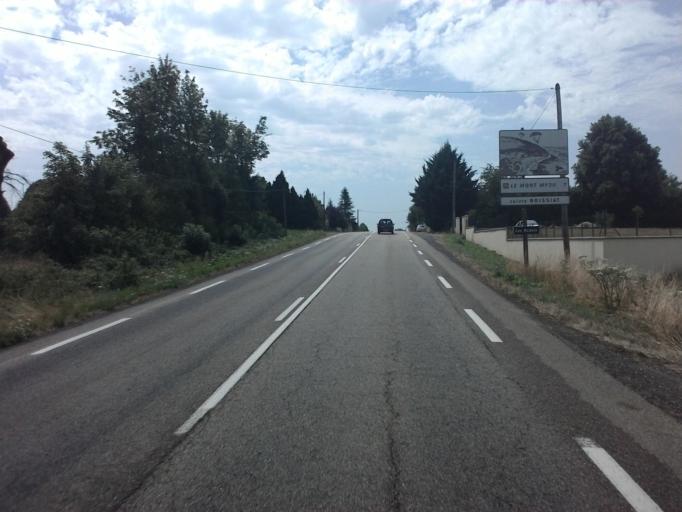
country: FR
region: Rhone-Alpes
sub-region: Departement de l'Ain
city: Coligny
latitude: 46.3389
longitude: 5.3188
